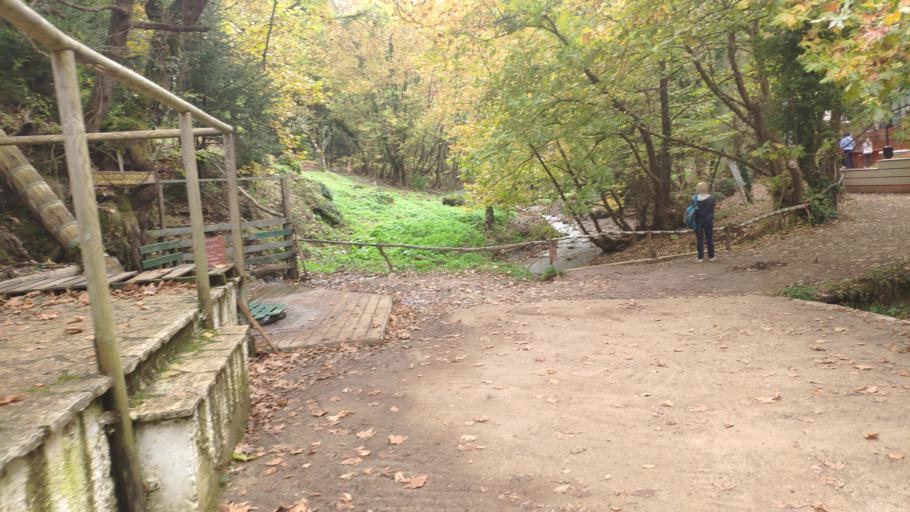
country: GR
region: Central Greece
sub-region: Nomos Fthiotidos
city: Stavros
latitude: 38.7379
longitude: 22.3409
